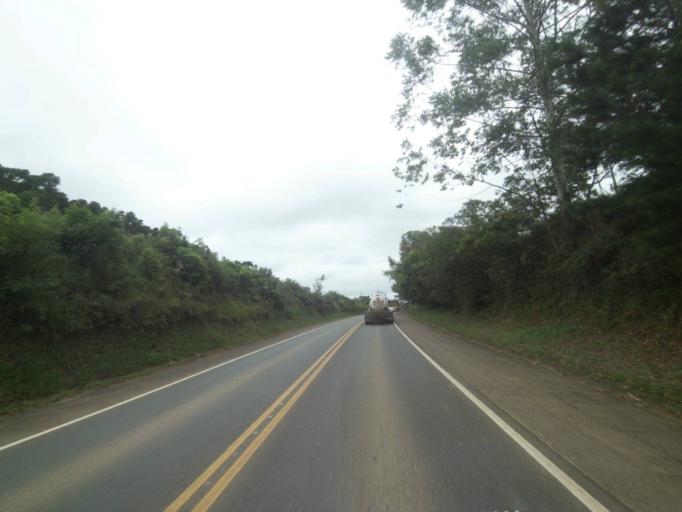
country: BR
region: Parana
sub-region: Telemaco Borba
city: Telemaco Borba
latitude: -24.3667
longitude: -50.6589
